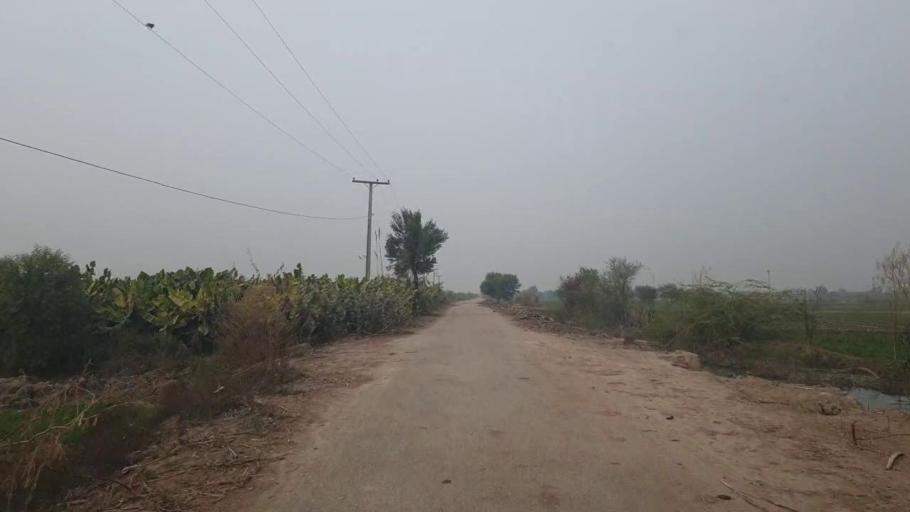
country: PK
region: Sindh
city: Tando Adam
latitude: 25.8199
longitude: 68.7138
